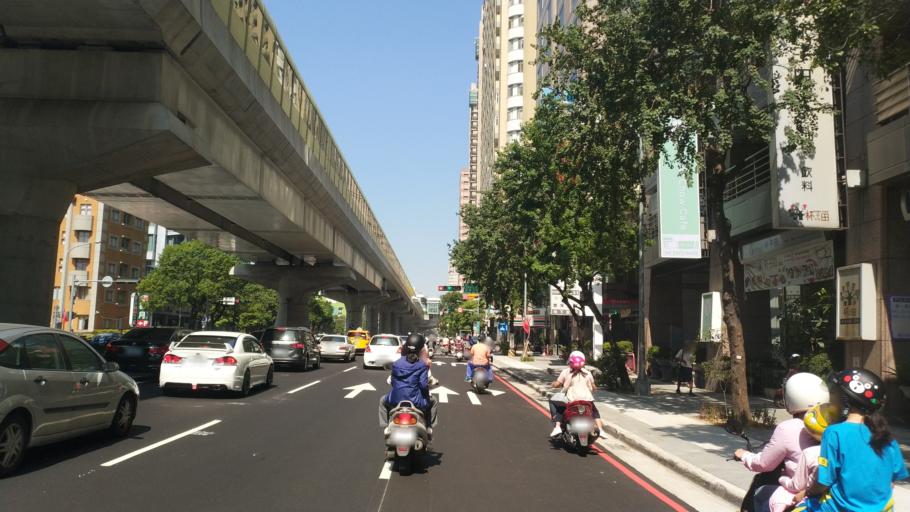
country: TW
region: Taiwan
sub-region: Taichung City
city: Taichung
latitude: 24.1421
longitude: 120.6469
